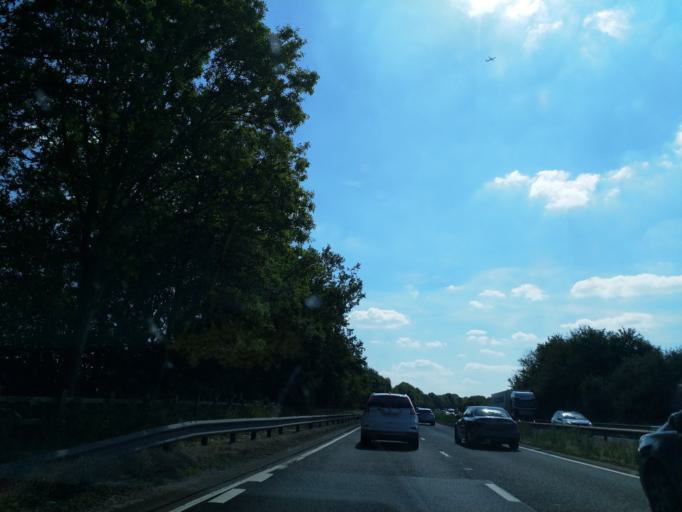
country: GB
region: England
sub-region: Warwickshire
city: Warwick
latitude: 52.3027
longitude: -1.5789
